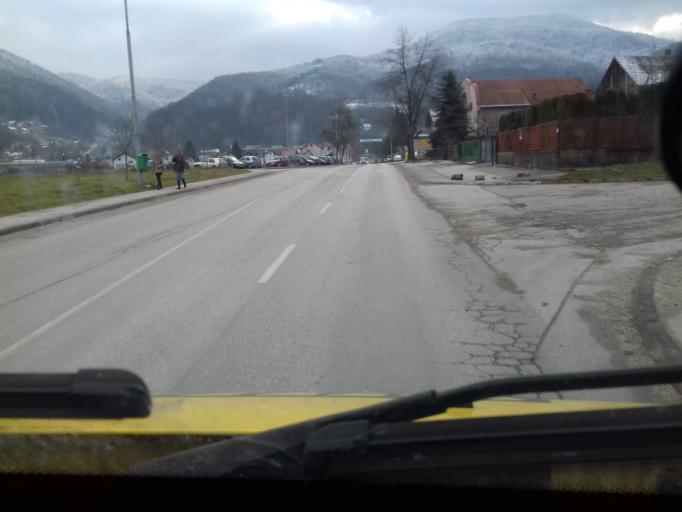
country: BA
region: Federation of Bosnia and Herzegovina
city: Zepce
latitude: 44.4279
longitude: 18.0404
